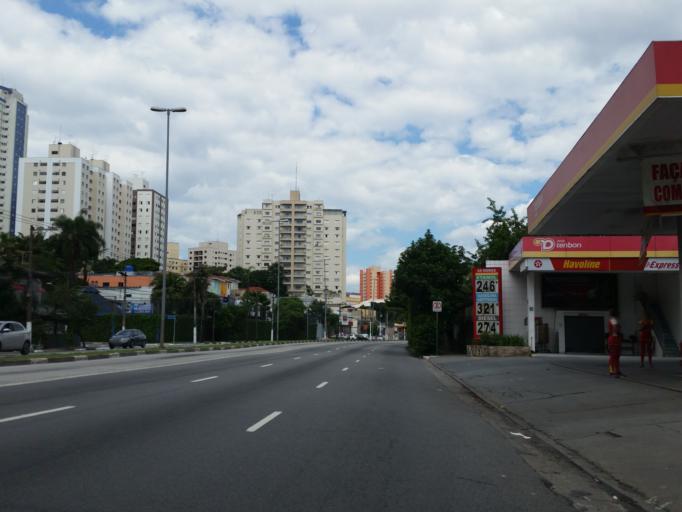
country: BR
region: Sao Paulo
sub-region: Diadema
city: Diadema
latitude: -23.6466
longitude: -46.6712
